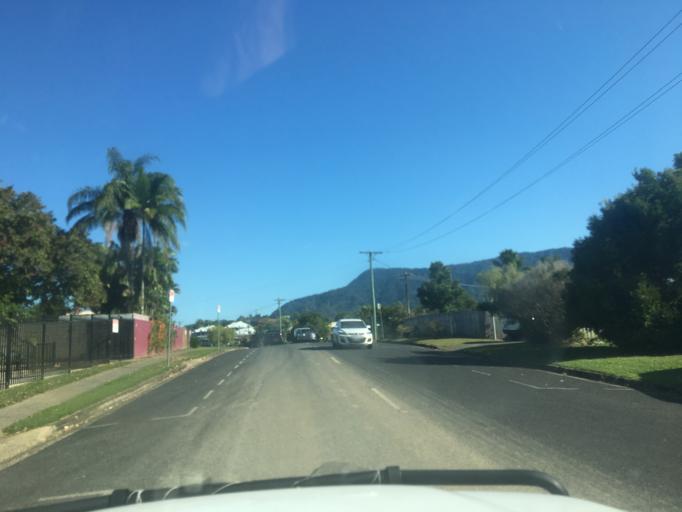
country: AU
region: Queensland
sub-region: Cairns
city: Woree
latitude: -16.9417
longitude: 145.7362
